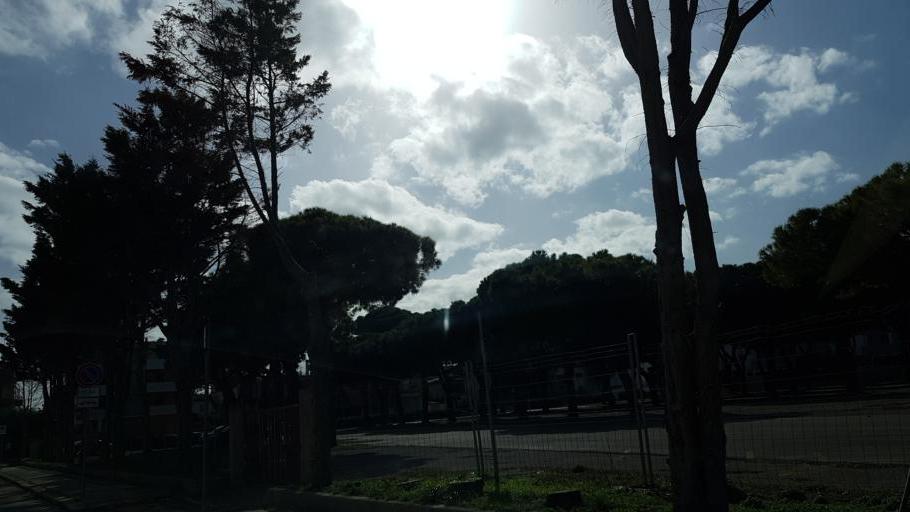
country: IT
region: Apulia
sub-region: Provincia di Brindisi
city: Brindisi
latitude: 40.6486
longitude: 17.9375
